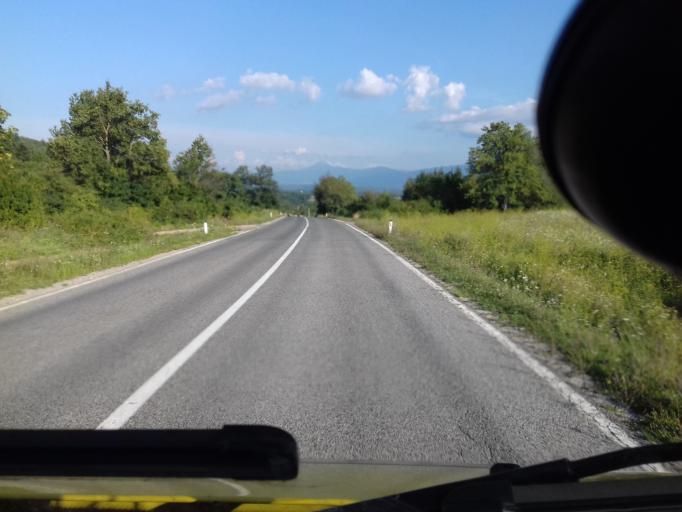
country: BA
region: Federation of Bosnia and Herzegovina
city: Orasac
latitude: 44.6528
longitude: 16.1579
